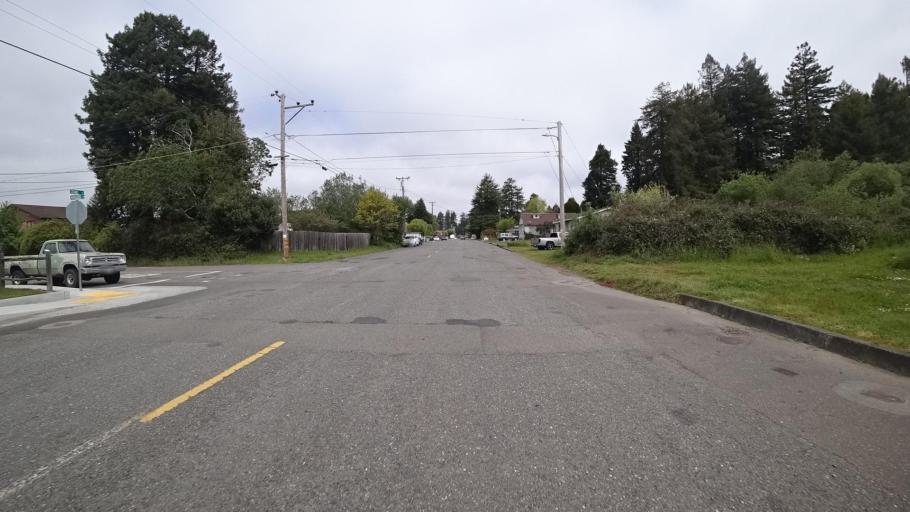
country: US
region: California
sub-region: Humboldt County
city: Cutten
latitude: 40.7676
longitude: -124.1413
